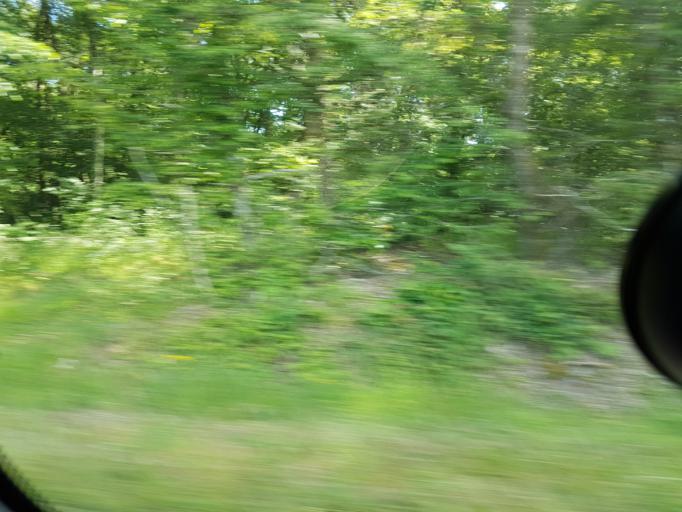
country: FR
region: Bourgogne
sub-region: Departement de Saone-et-Loire
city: Autun
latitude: 47.0544
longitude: 4.2852
